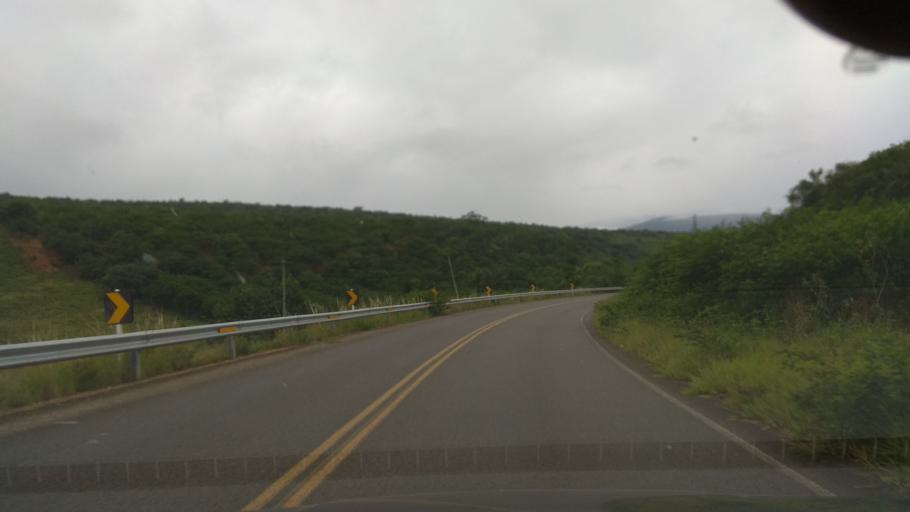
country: BR
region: Bahia
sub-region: Santa Ines
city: Santa Ines
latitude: -13.2528
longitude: -39.7824
